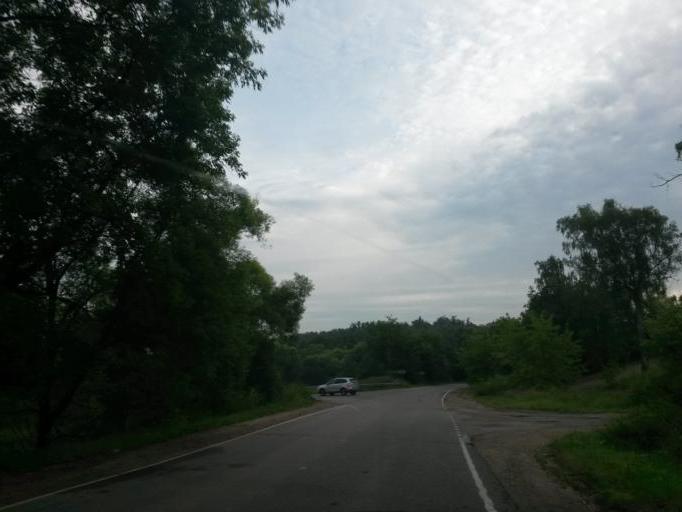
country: RU
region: Moskovskaya
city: Lyubuchany
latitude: 55.2746
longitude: 37.6230
